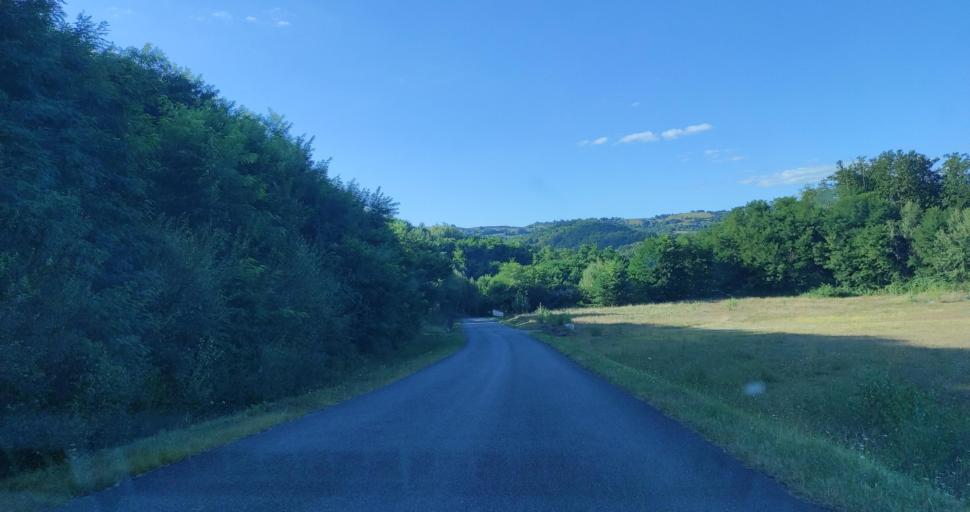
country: FR
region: Midi-Pyrenees
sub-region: Departement de l'Aveyron
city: Firmi
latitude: 44.5326
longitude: 2.3178
